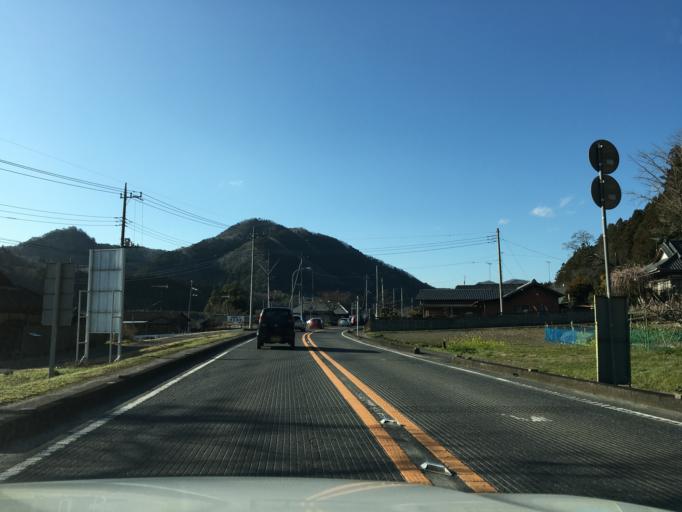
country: JP
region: Ibaraki
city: Omiya
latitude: 36.6578
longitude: 140.3935
